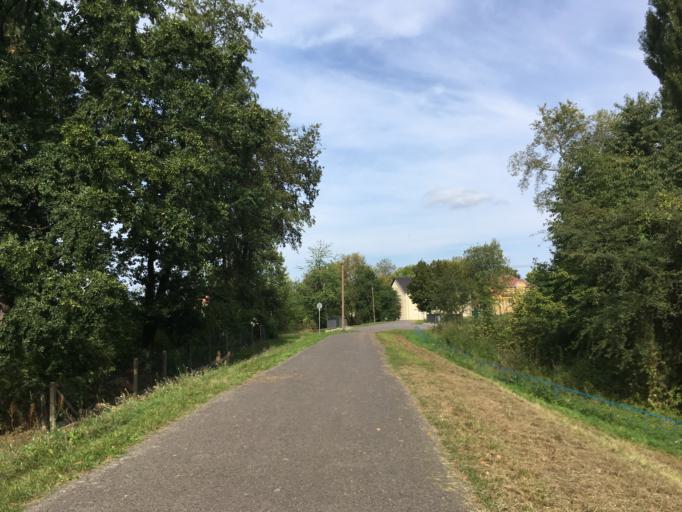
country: DE
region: Brandenburg
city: Schenkendobern
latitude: 51.8811
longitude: 14.6512
